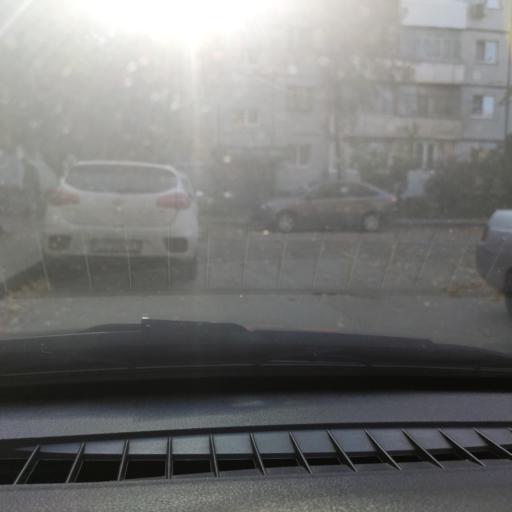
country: RU
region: Samara
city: Tol'yatti
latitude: 53.5254
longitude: 49.2714
